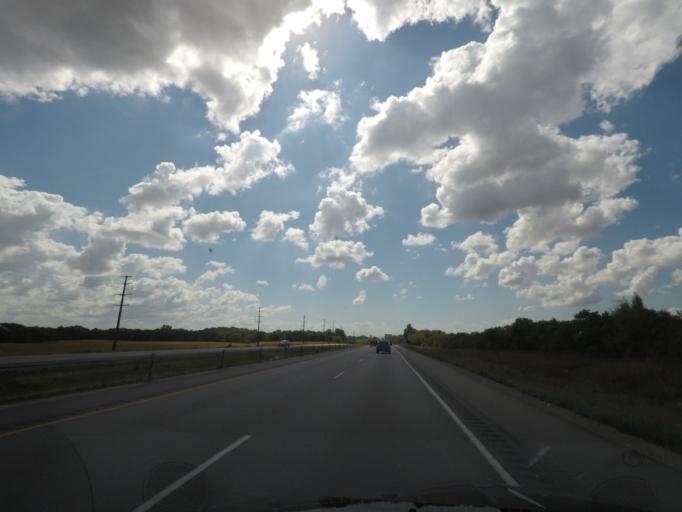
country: US
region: Iowa
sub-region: Story County
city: Huxley
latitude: 41.9112
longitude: -93.5707
